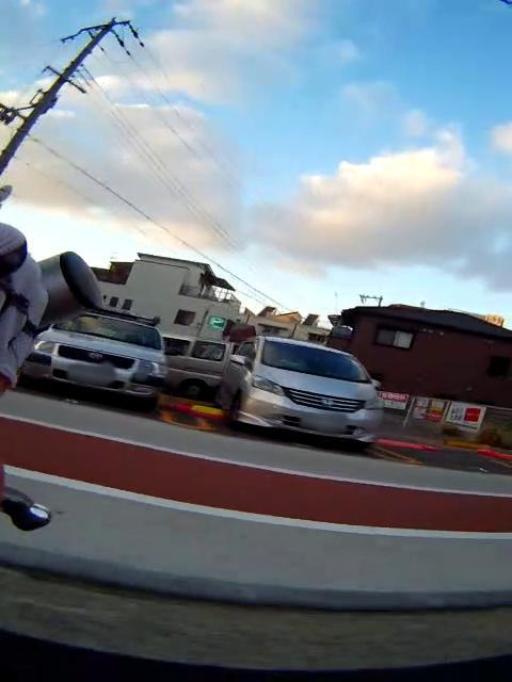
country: JP
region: Osaka
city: Osaka-shi
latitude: 34.7212
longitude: 135.4874
